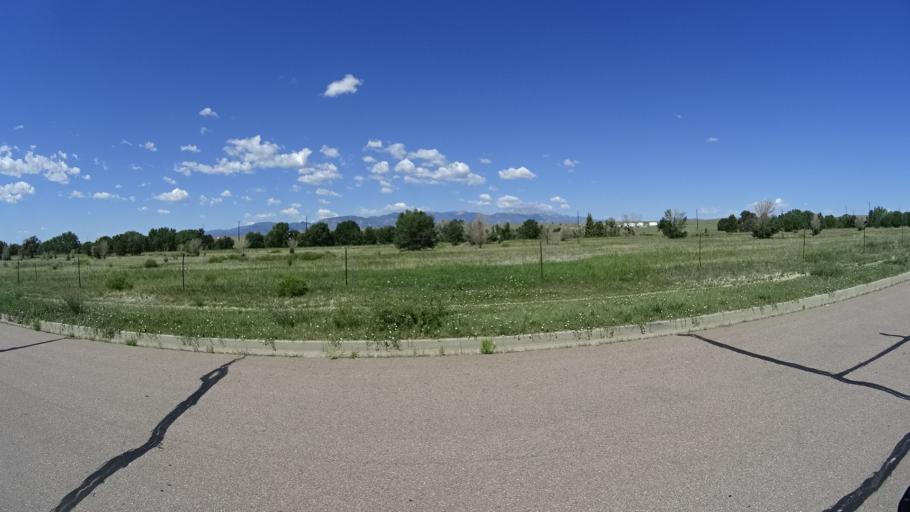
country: US
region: Colorado
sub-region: El Paso County
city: Security-Widefield
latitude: 38.7758
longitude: -104.6576
